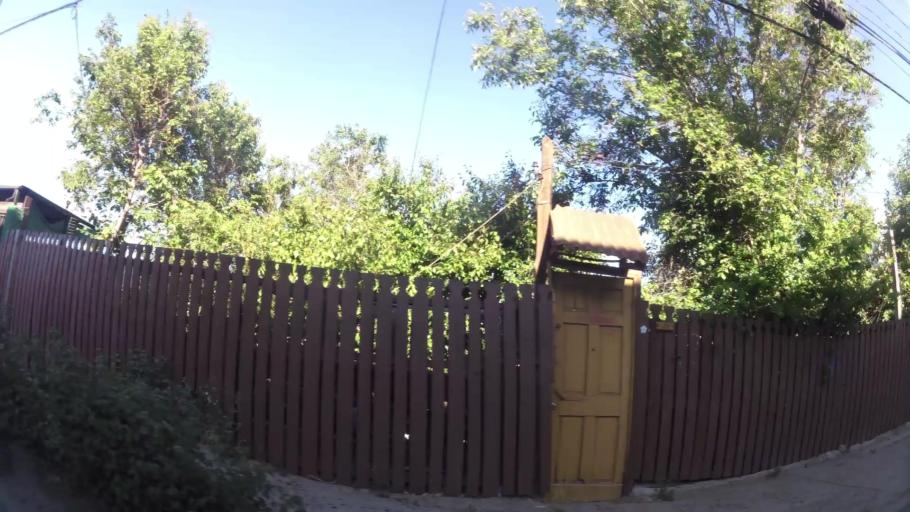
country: CL
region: Valparaiso
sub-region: Provincia de Valparaiso
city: Valparaiso
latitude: -33.0534
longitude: -71.6245
